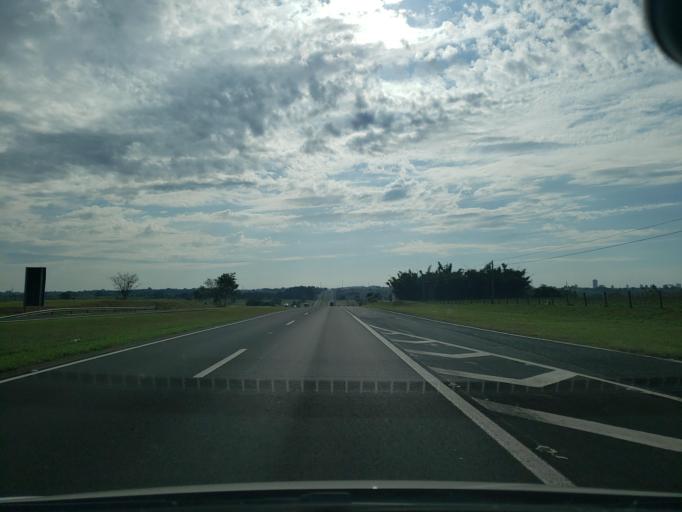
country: BR
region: Sao Paulo
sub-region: Birigui
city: Birigui
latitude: -21.3376
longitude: -50.3269
